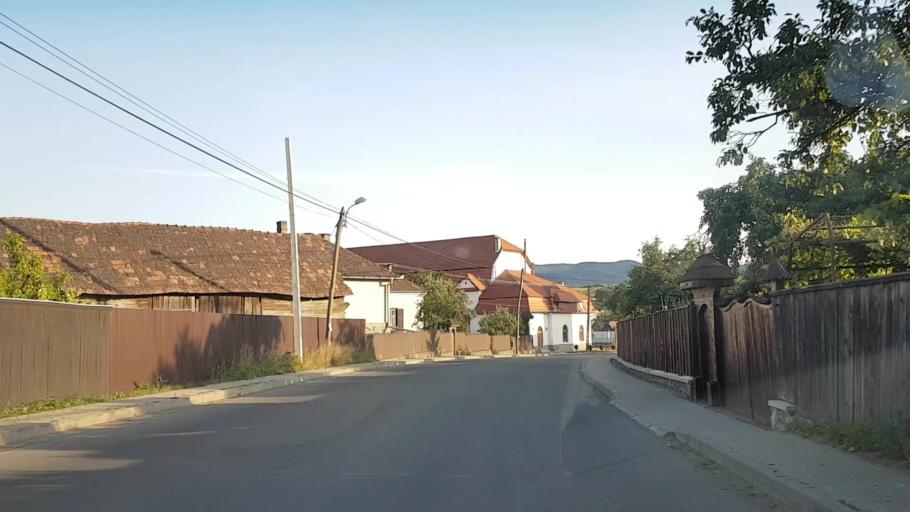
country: RO
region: Harghita
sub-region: Comuna Praid
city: Praid
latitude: 46.5547
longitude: 25.1290
